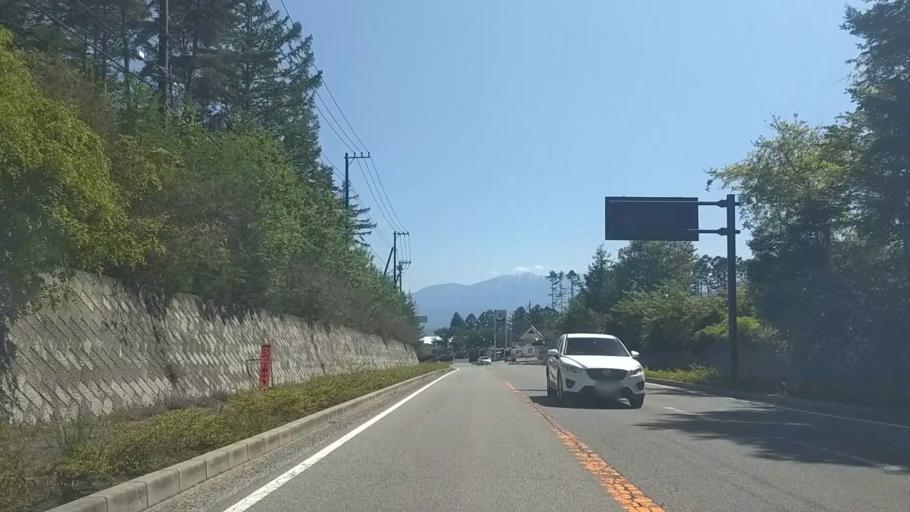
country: JP
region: Yamanashi
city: Nirasaki
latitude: 35.8905
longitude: 138.4399
